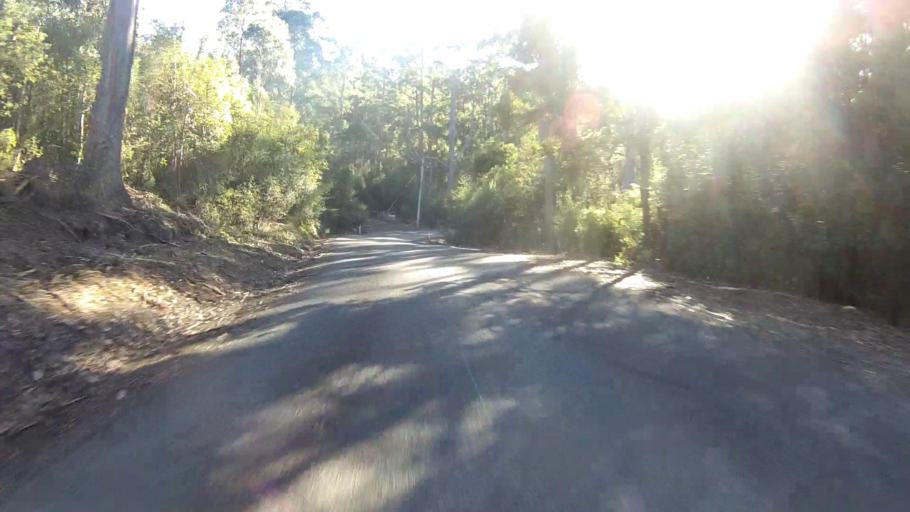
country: AU
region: Tasmania
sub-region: Sorell
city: Sorell
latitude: -43.0082
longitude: 147.9304
